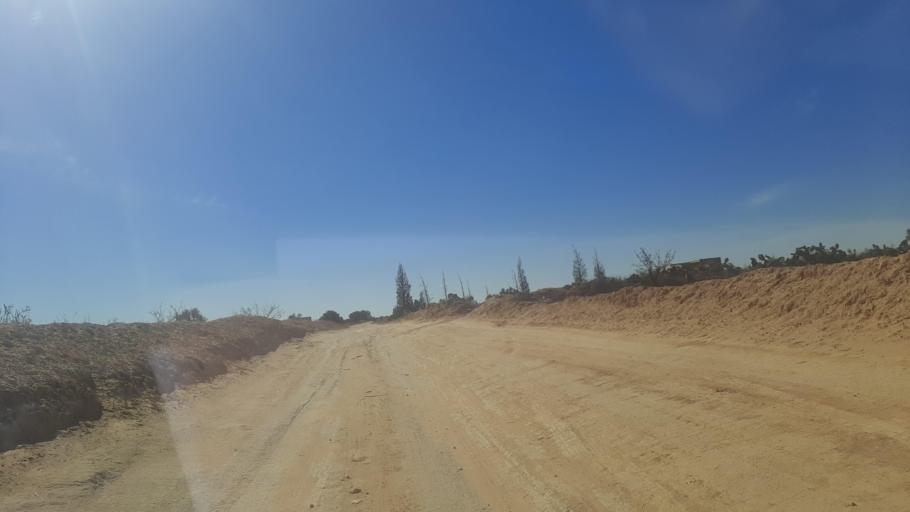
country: TN
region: Safaqis
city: Sfax
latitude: 34.8497
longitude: 10.5621
